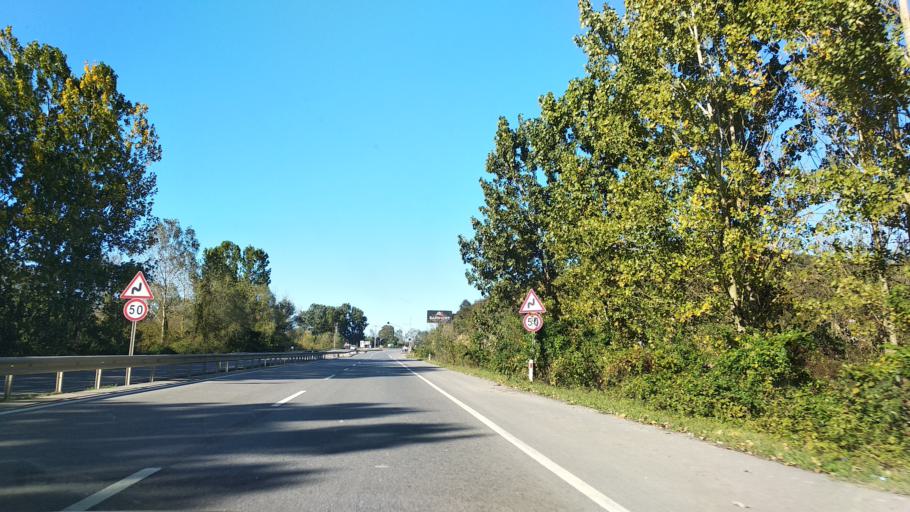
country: TR
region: Sakarya
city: Karasu
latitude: 41.0779
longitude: 30.6461
